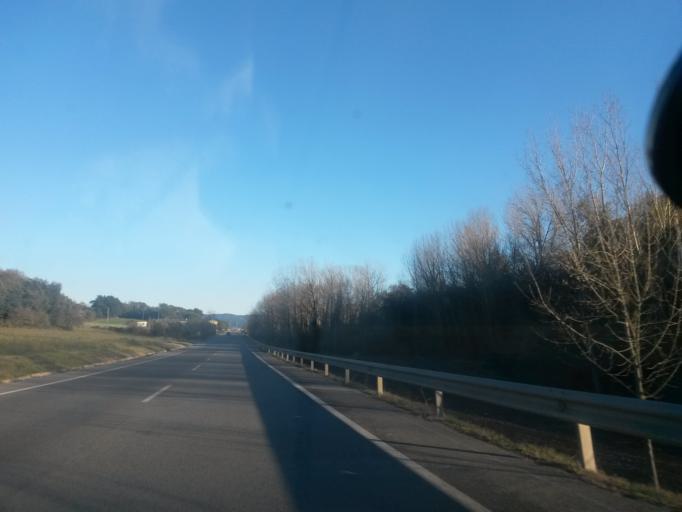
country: ES
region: Catalonia
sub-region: Provincia de Girona
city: Aiguaviva
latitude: 41.9384
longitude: 2.7694
